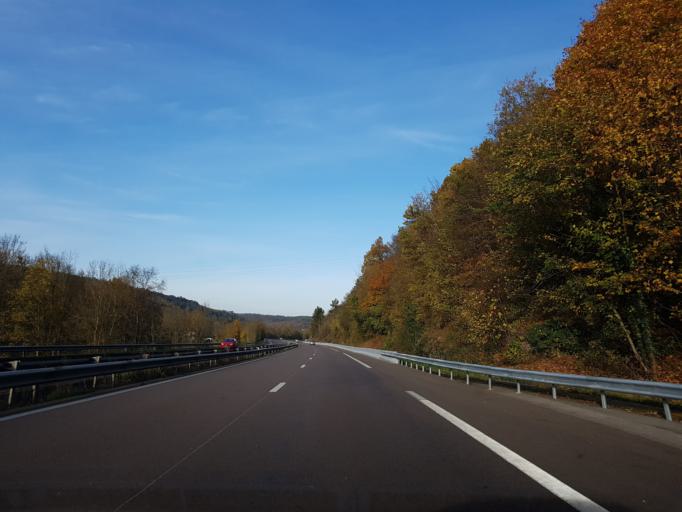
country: FR
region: Bourgogne
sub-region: Departement de la Cote-d'Or
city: Velars-sur-Ouche
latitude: 47.3221
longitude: 4.9324
